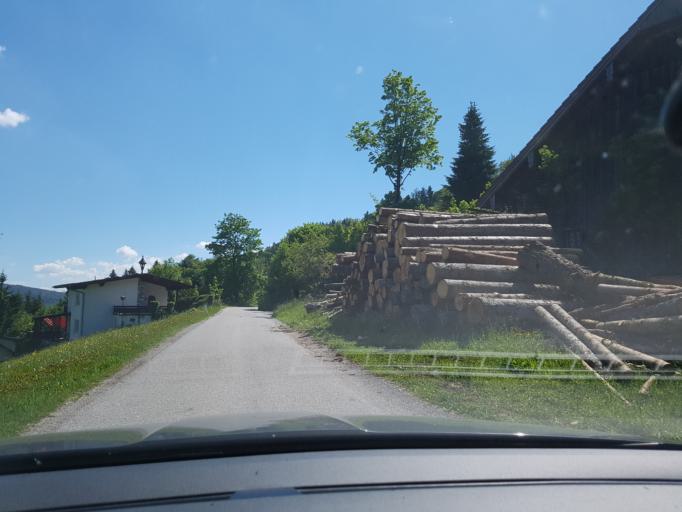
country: AT
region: Salzburg
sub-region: Politischer Bezirk Salzburg-Umgebung
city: Koppl
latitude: 47.7909
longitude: 13.1180
